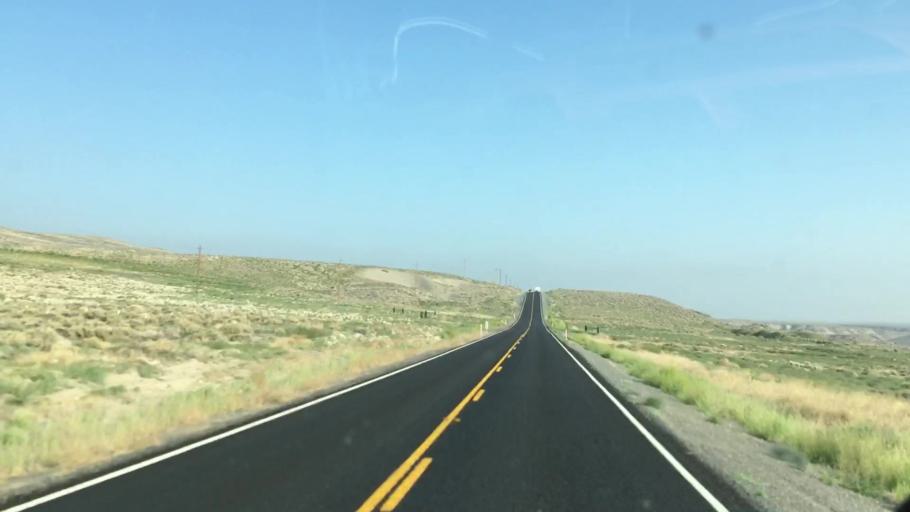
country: US
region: Nevada
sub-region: Lyon County
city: Fernley
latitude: 39.7594
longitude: -119.3385
